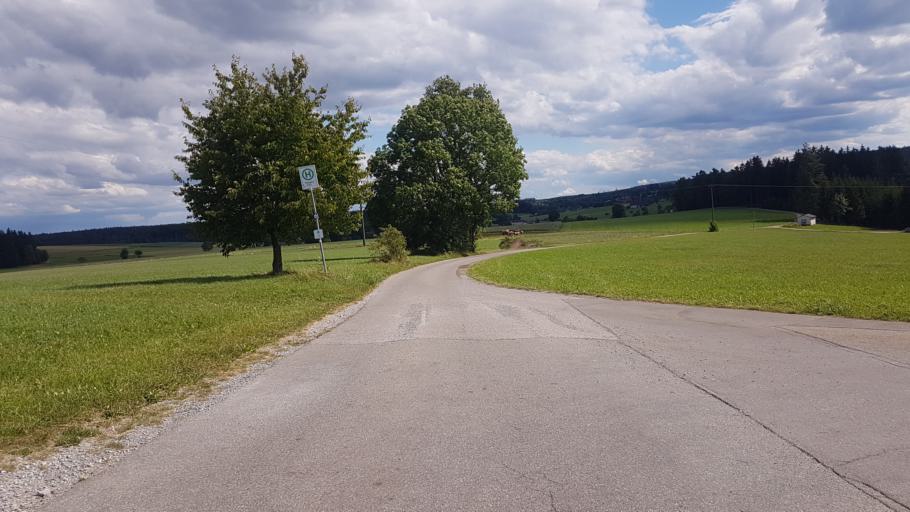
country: DE
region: Baden-Wuerttemberg
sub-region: Freiburg Region
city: Hardt
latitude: 48.1688
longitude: 8.4072
